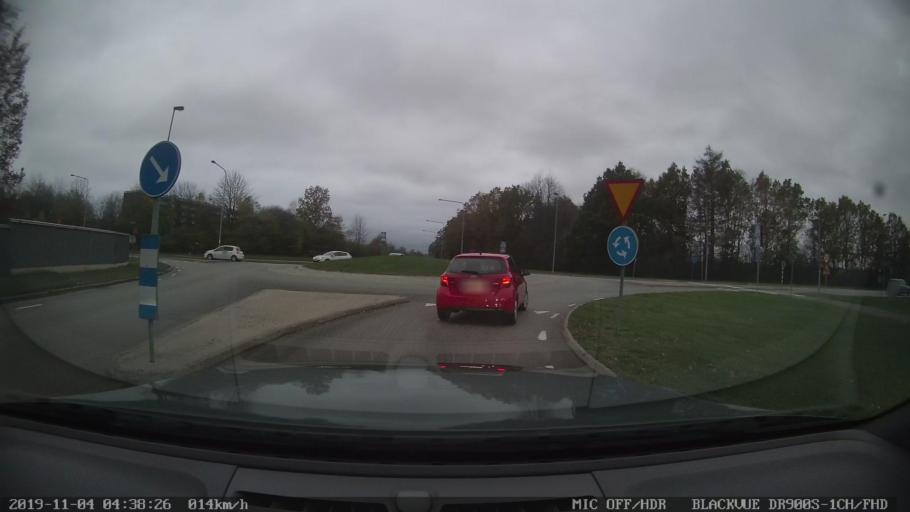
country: SE
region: Skane
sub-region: Helsingborg
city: Helsingborg
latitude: 56.0538
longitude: 12.7361
